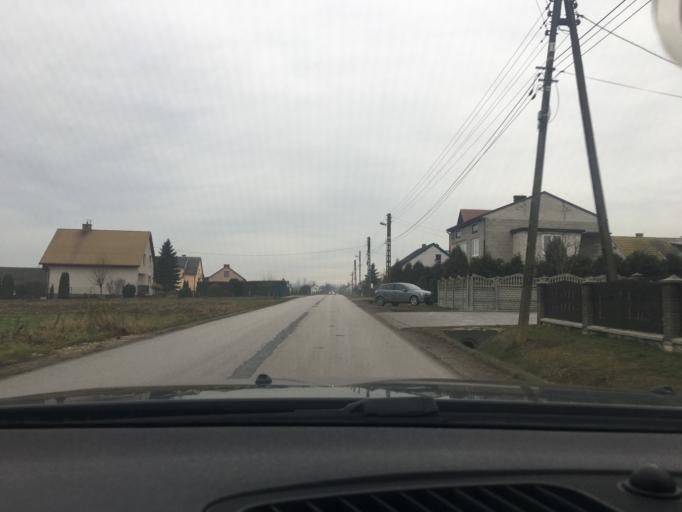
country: PL
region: Swietokrzyskie
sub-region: Powiat jedrzejowski
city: Jedrzejow
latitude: 50.6404
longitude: 20.3683
